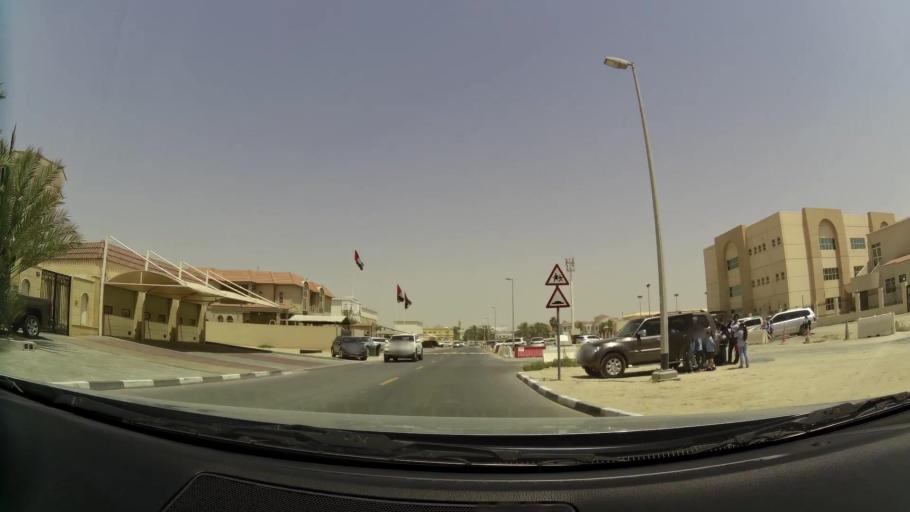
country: AE
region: Dubai
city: Dubai
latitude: 25.1340
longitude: 55.2046
